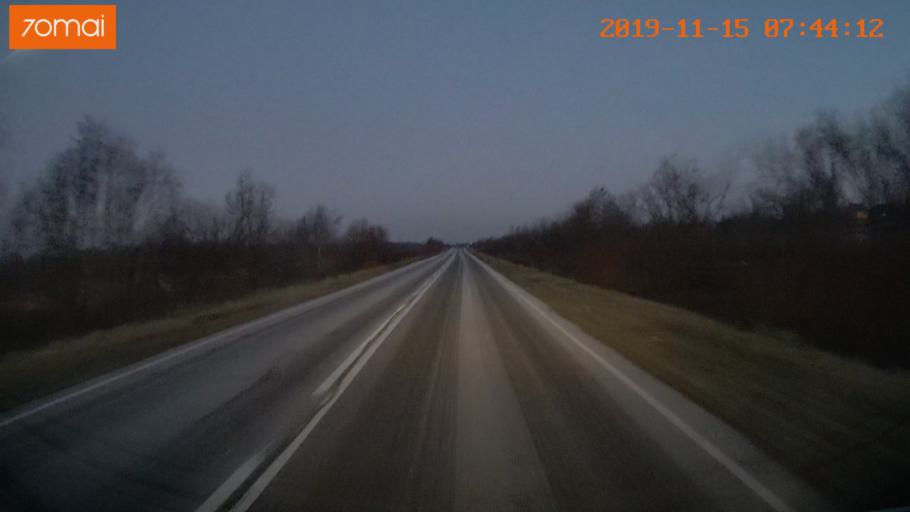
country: RU
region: Vologda
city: Sheksna
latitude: 58.8107
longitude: 38.3167
